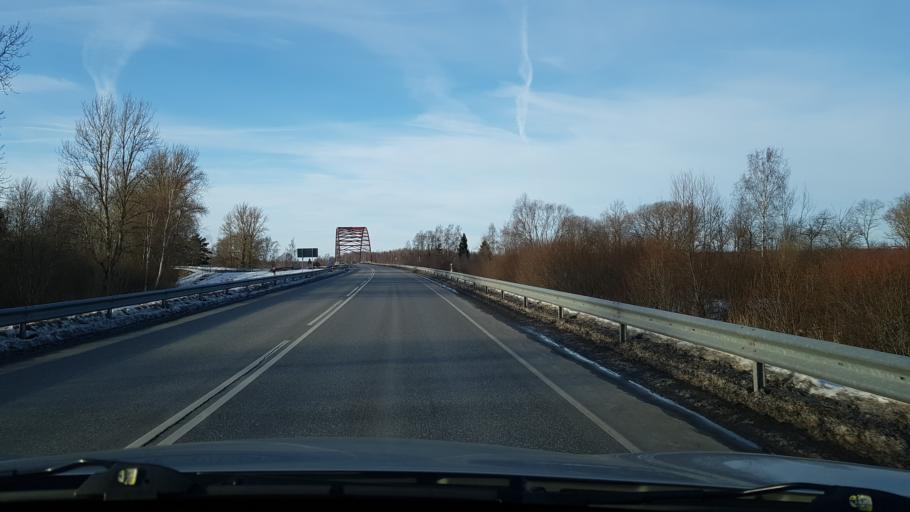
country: EE
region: Tartu
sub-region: Puhja vald
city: Puhja
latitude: 58.3833
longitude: 26.1385
